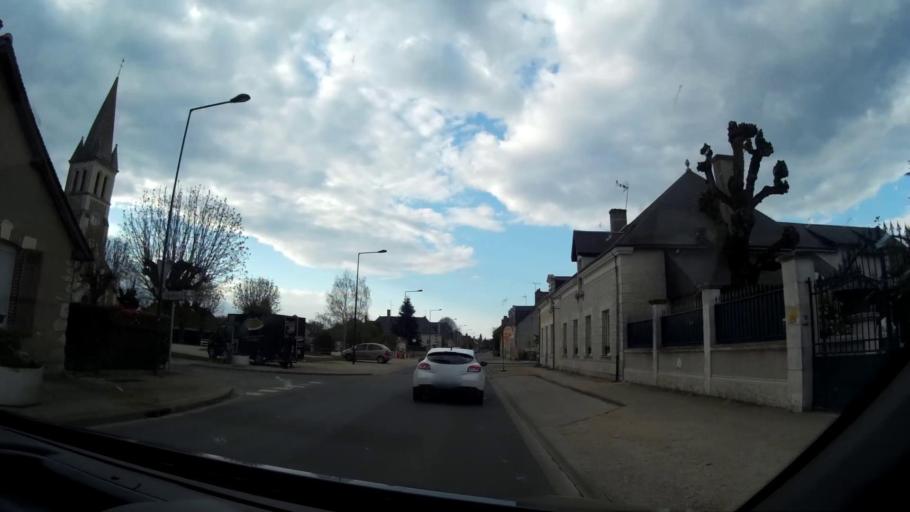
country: FR
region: Centre
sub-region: Departement du Loir-et-Cher
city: Cormeray
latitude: 47.4890
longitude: 1.4076
